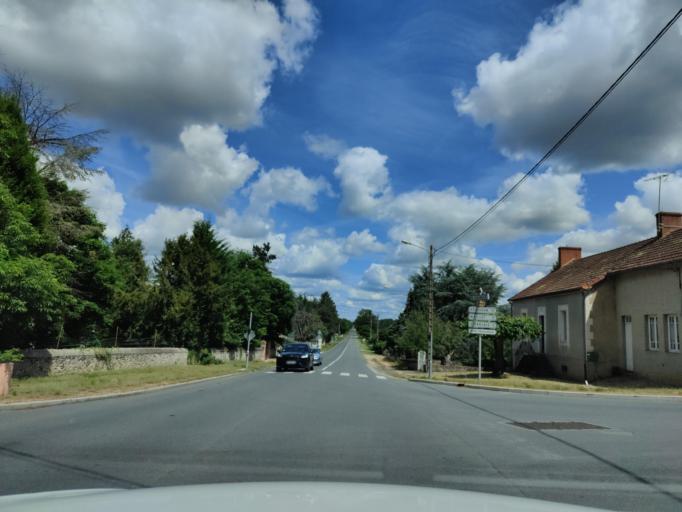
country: FR
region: Auvergne
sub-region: Departement de l'Allier
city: Estivareilles
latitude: 46.4629
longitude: 2.6155
